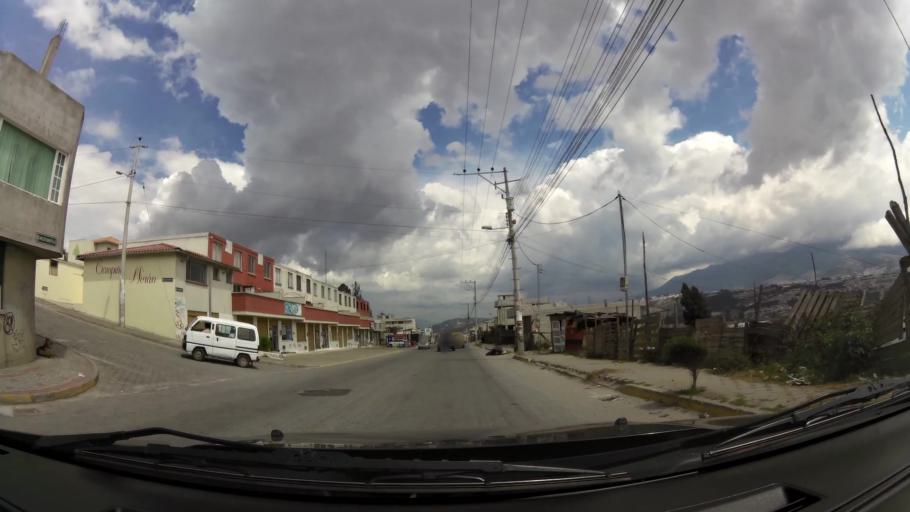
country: EC
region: Pichincha
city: Quito
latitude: -0.0735
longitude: -78.4345
